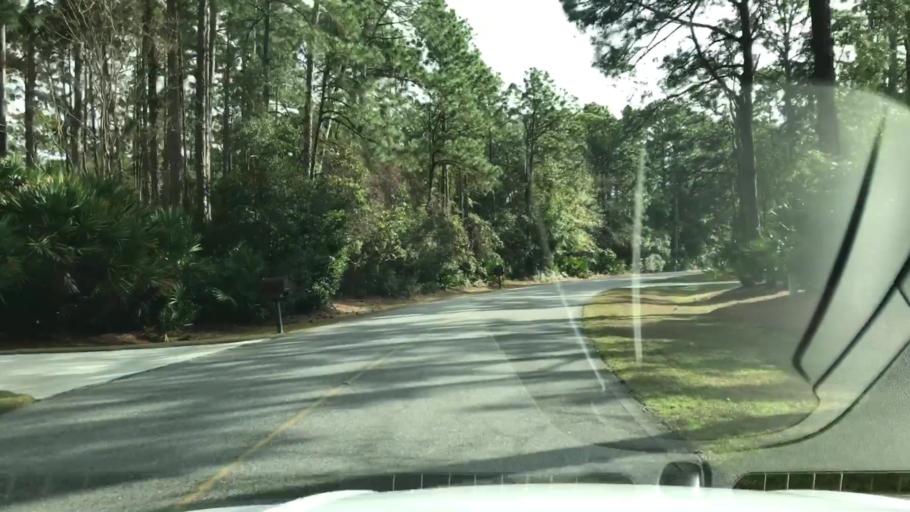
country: US
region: South Carolina
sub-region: Beaufort County
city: Hilton Head Island
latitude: 32.2443
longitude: -80.7071
